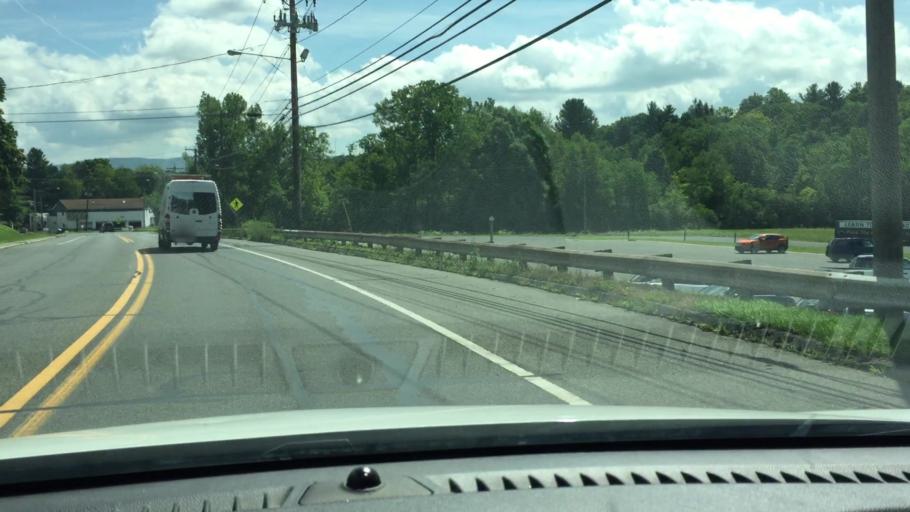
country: US
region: Massachusetts
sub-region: Berkshire County
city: Pittsfield
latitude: 42.4400
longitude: -73.2859
